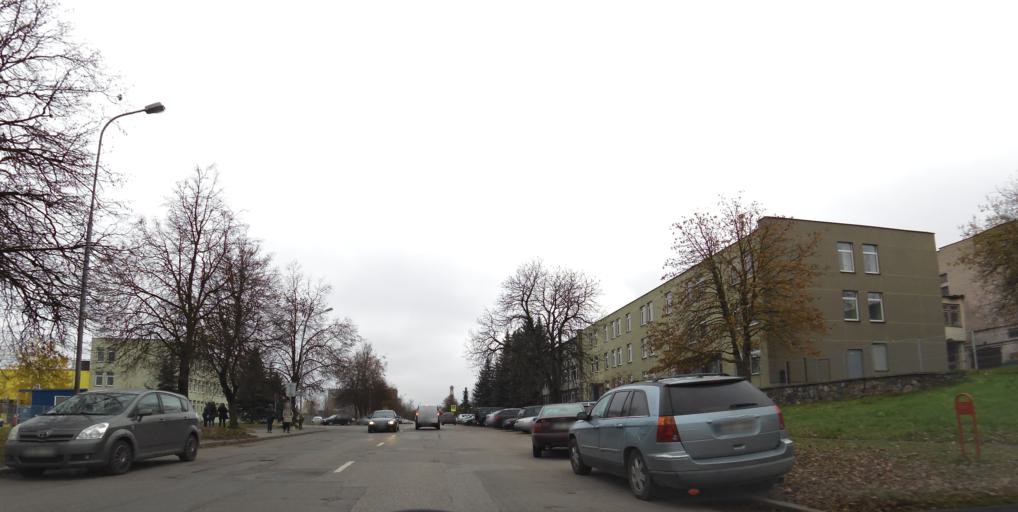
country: LT
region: Vilnius County
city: Vilkpede
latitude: 54.6402
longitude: 25.2667
